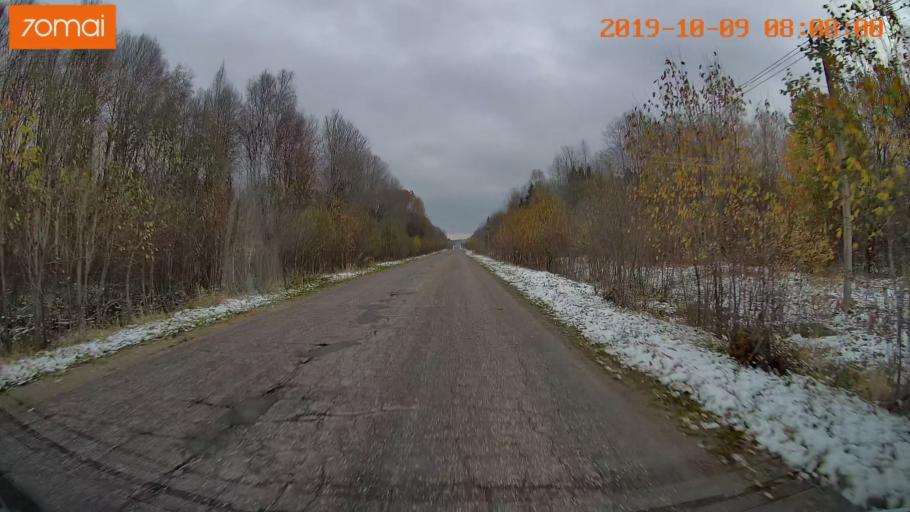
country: RU
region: Jaroslavl
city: Kukoboy
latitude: 58.7014
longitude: 40.0889
